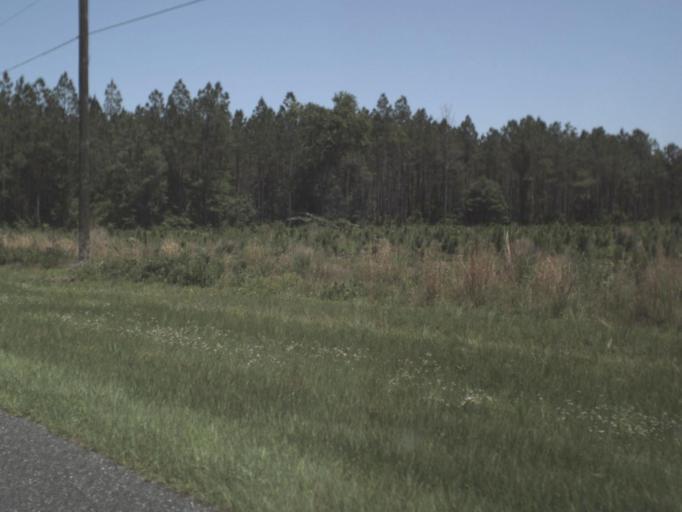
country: US
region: Florida
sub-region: Baker County
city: Macclenny
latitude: 30.2362
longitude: -82.3112
